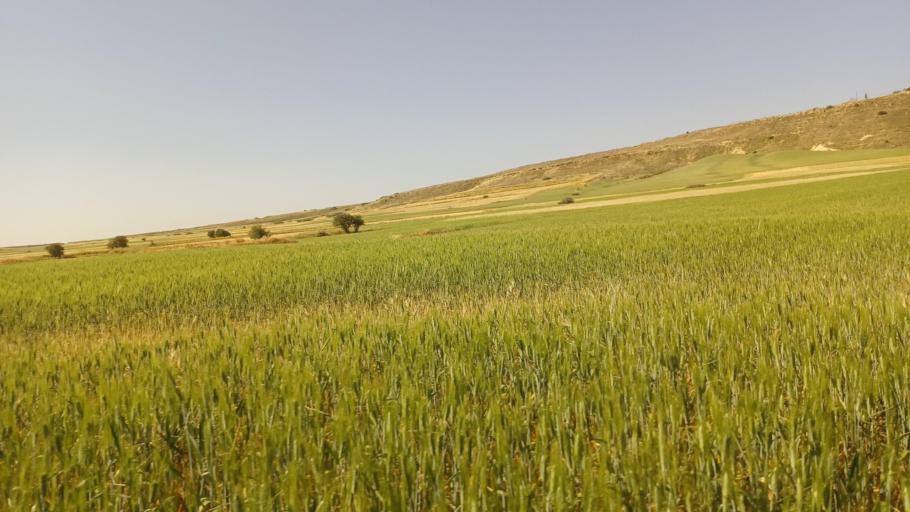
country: CY
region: Lefkosia
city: Mammari
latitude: 35.1690
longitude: 33.2387
